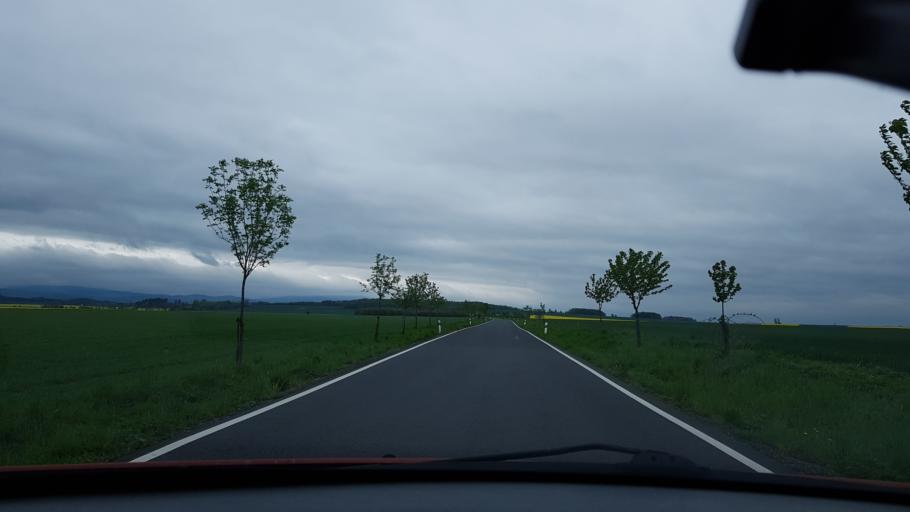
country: CZ
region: Olomoucky
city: Vidnava
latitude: 50.3786
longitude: 17.1649
